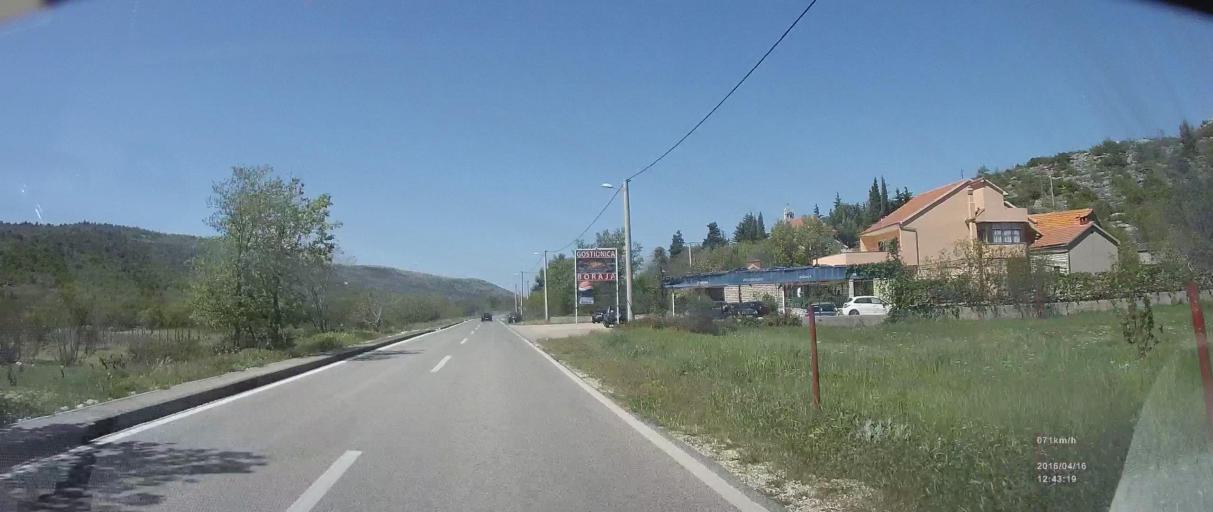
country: HR
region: Sibensko-Kniniska
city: Rogoznica
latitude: 43.6319
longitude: 16.0767
